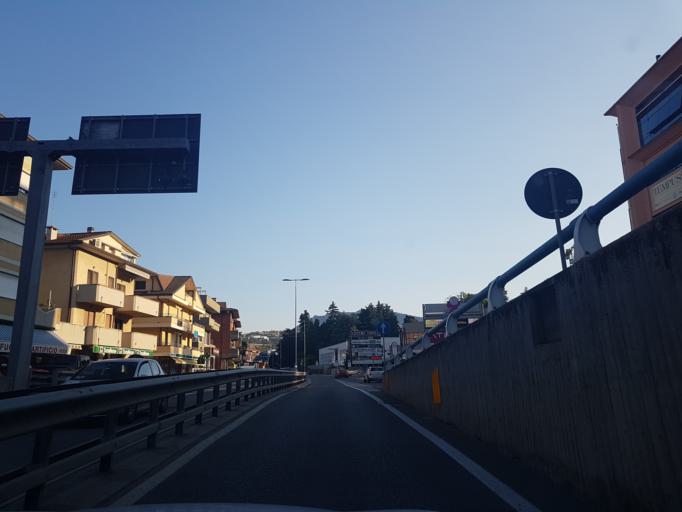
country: SM
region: Serravalle
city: Serravalle
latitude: 43.9770
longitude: 12.4871
